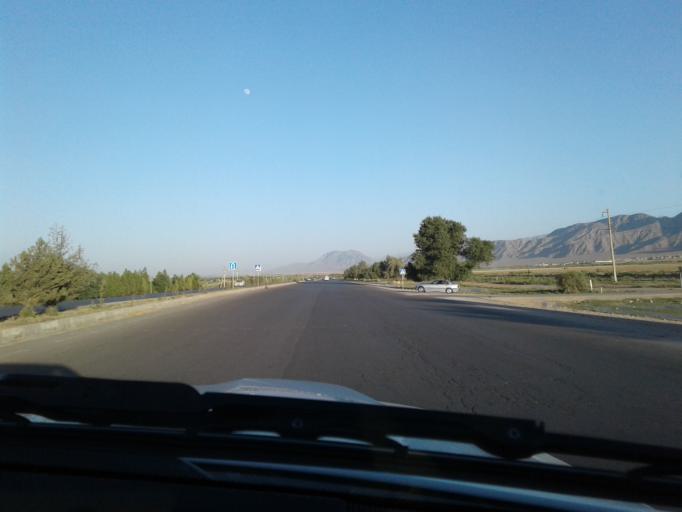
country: TM
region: Ahal
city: Arcabil
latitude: 38.2176
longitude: 57.8044
